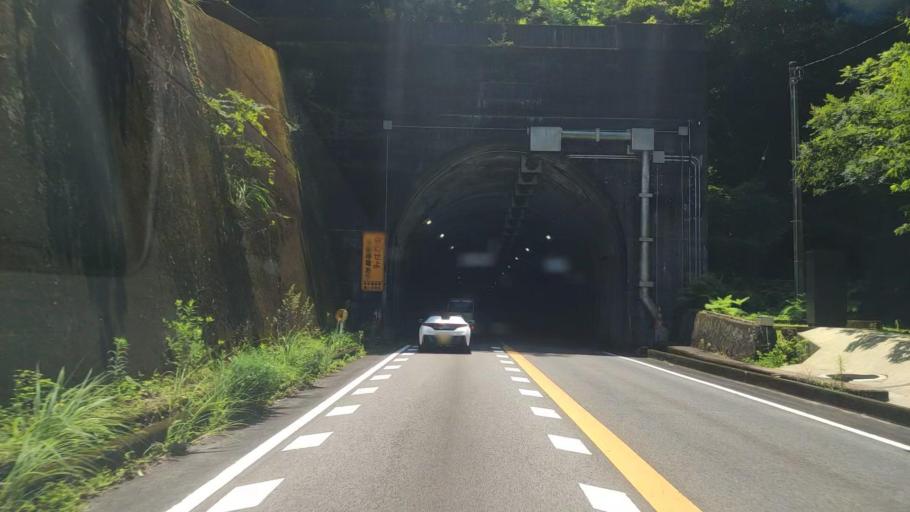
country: JP
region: Mie
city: Owase
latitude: 34.1571
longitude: 136.2664
